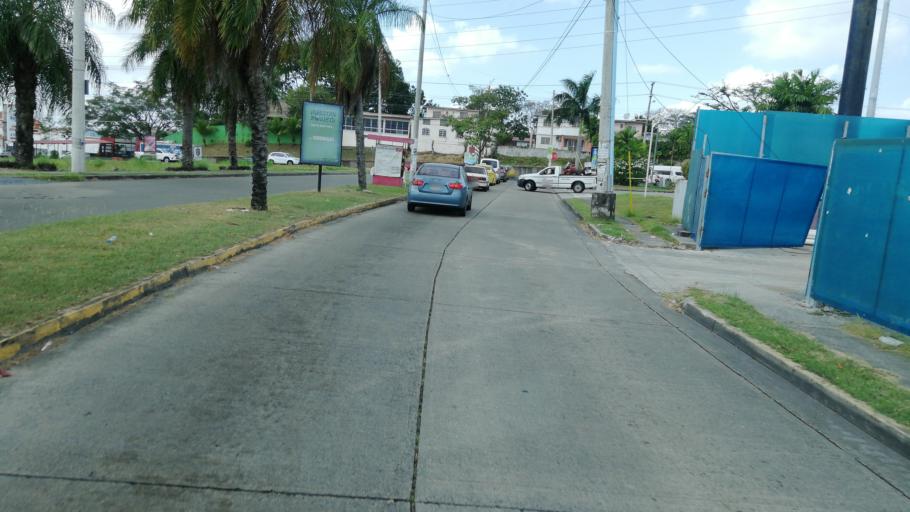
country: PA
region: Panama
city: San Miguelito
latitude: 9.0527
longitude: -79.4601
